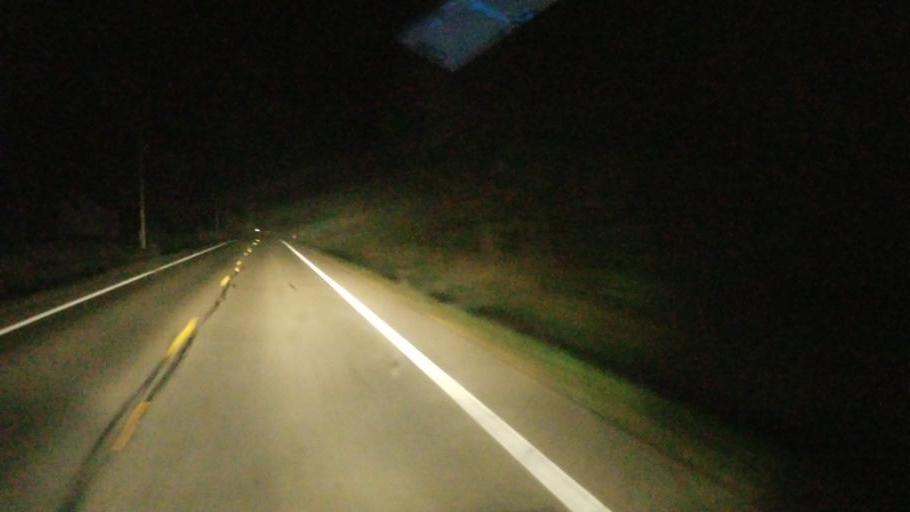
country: US
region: Ohio
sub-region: Morrow County
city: Cardington
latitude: 40.5855
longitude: -82.9791
